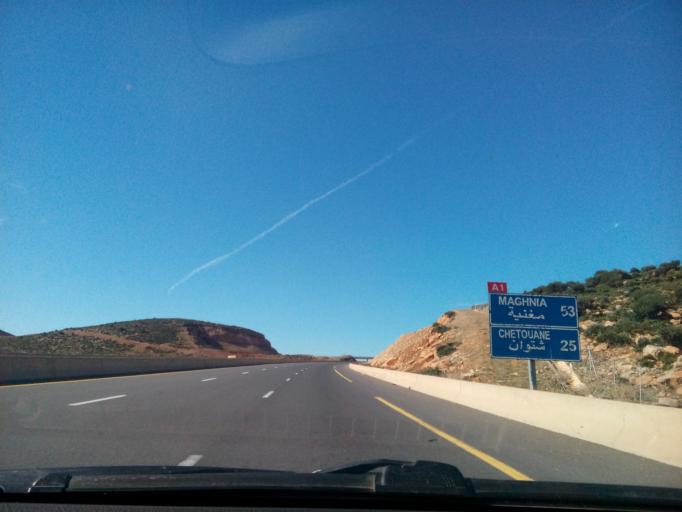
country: DZ
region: Tlemcen
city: Sidi Abdelli
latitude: 35.0196
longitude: -1.1338
